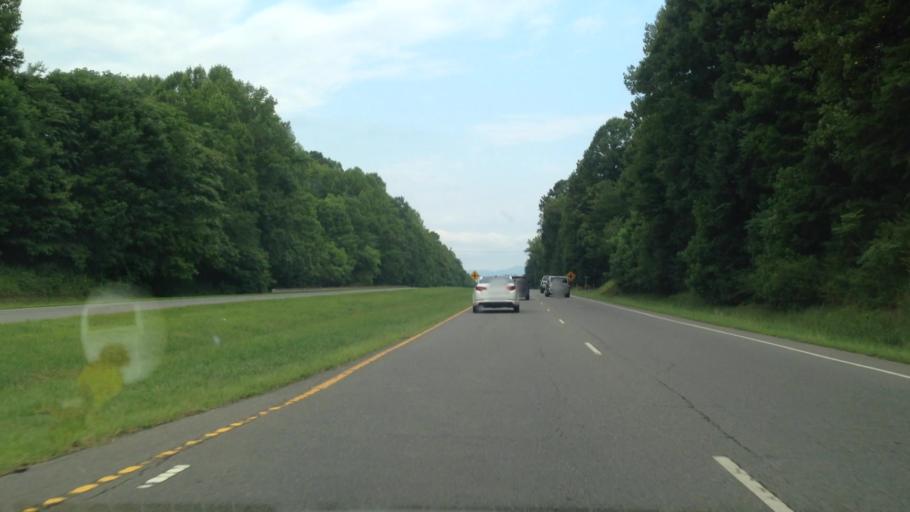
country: US
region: North Carolina
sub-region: Surry County
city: Mount Airy
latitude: 36.4736
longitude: -80.5799
